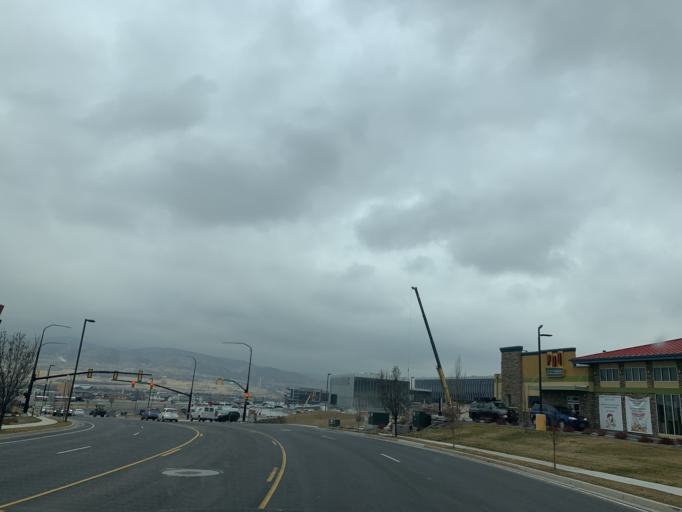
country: US
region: Utah
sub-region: Utah County
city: Lehi
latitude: 40.4327
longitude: -111.8874
